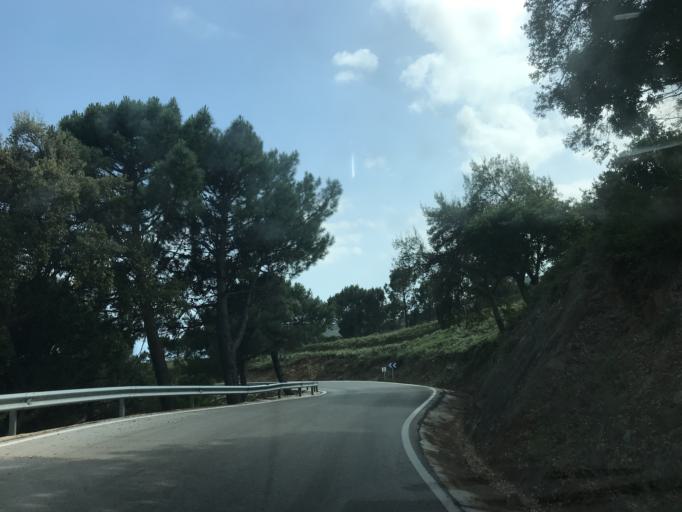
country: ES
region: Andalusia
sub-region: Provincia de Malaga
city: Estepona
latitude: 36.4879
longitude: -5.1799
